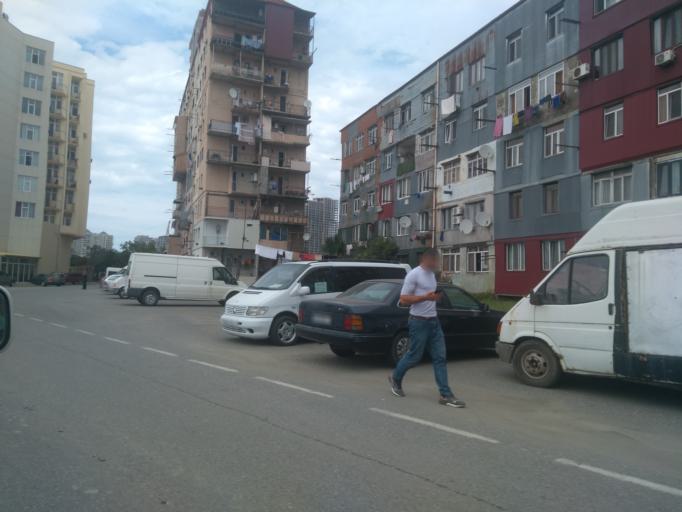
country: GE
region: Ajaria
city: Batumi
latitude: 41.6343
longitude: 41.6230
